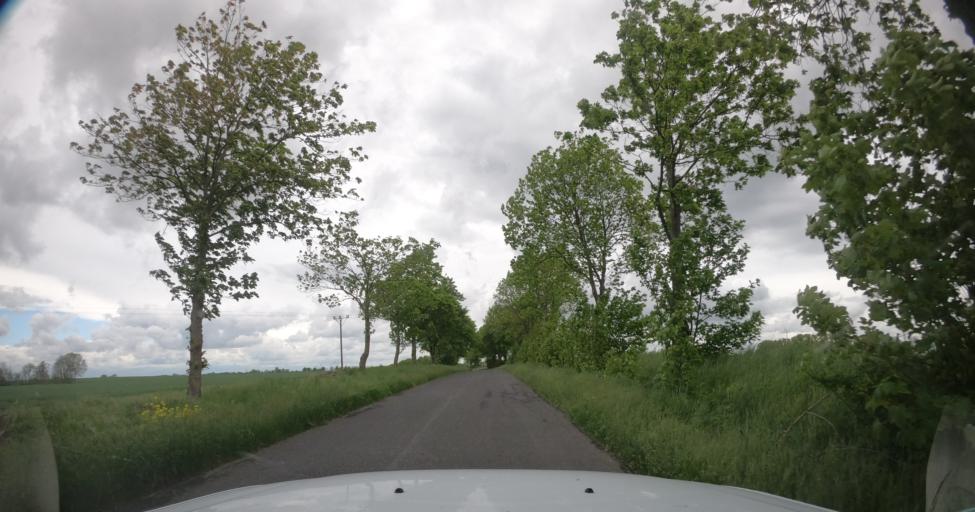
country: PL
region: West Pomeranian Voivodeship
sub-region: Powiat pyrzycki
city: Kozielice
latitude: 53.1190
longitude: 14.8082
